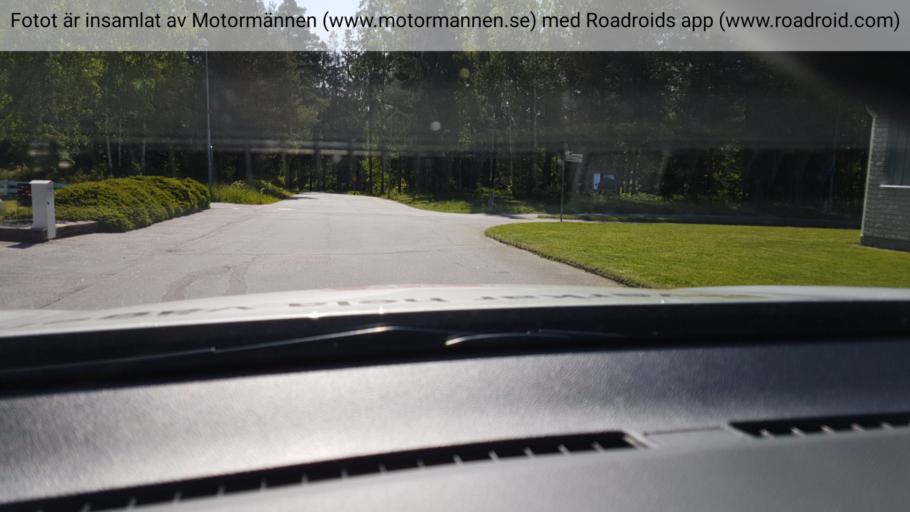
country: SE
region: Vaestra Goetaland
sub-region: Tibro Kommun
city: Tibro
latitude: 58.4228
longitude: 14.1430
